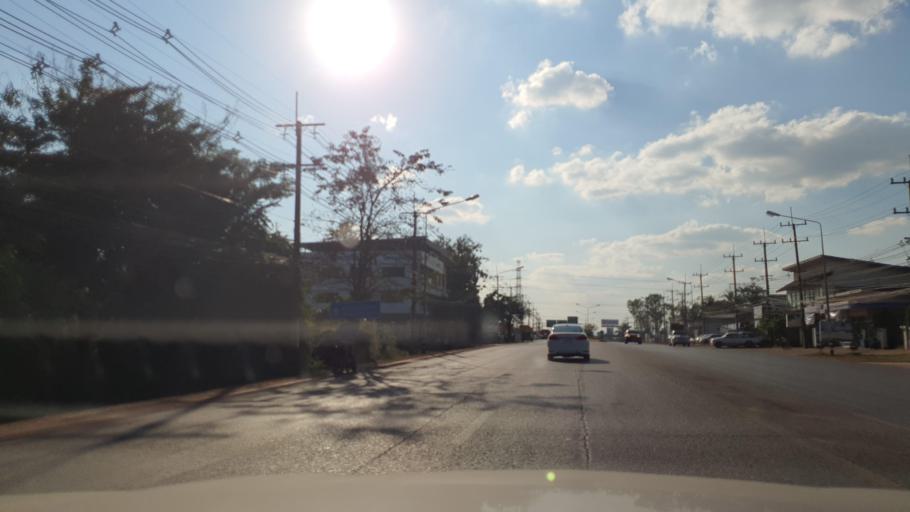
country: TH
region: Sakon Nakhon
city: Sakon Nakhon
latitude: 17.1431
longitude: 104.1148
